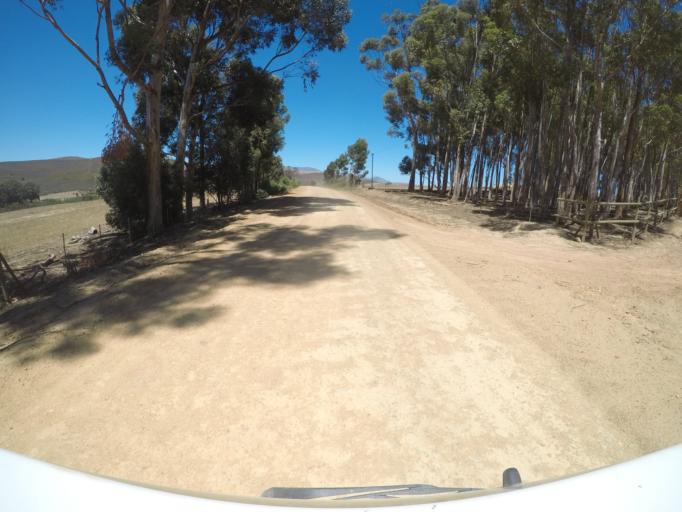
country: ZA
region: Western Cape
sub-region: Overberg District Municipality
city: Caledon
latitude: -34.1886
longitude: 19.2245
